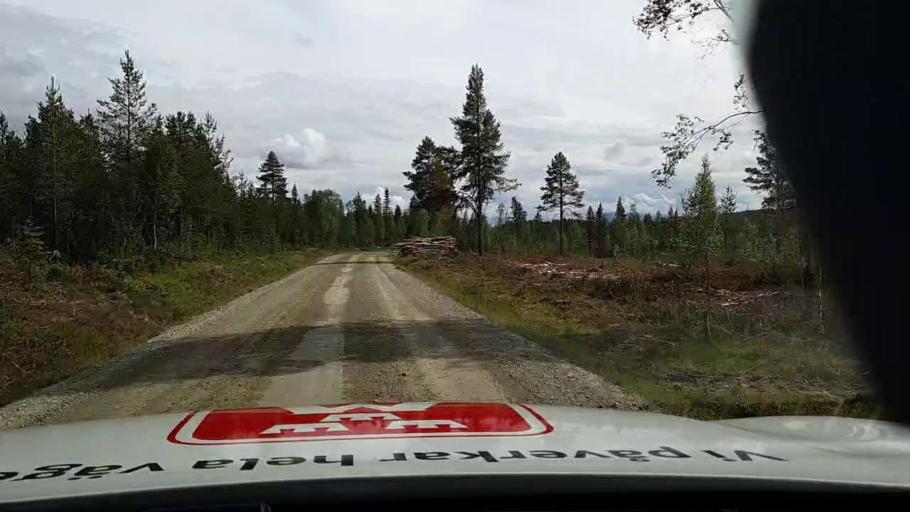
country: SE
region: Jaemtland
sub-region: Are Kommun
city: Jarpen
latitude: 62.5277
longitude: 13.4864
